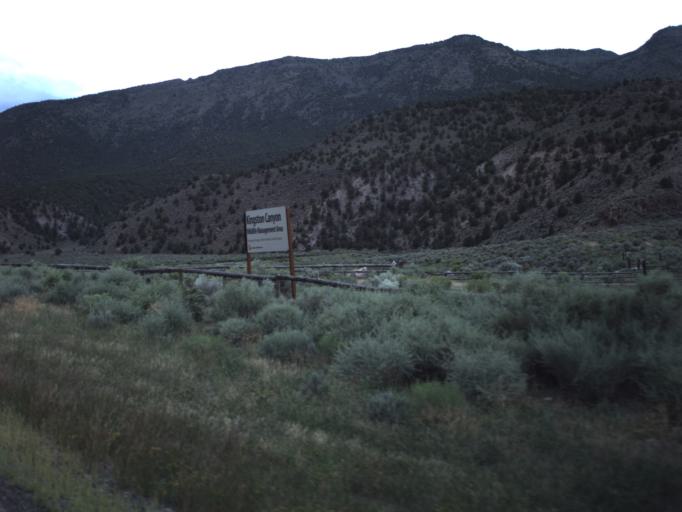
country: US
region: Utah
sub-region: Piute County
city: Junction
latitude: 38.1808
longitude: -112.0795
